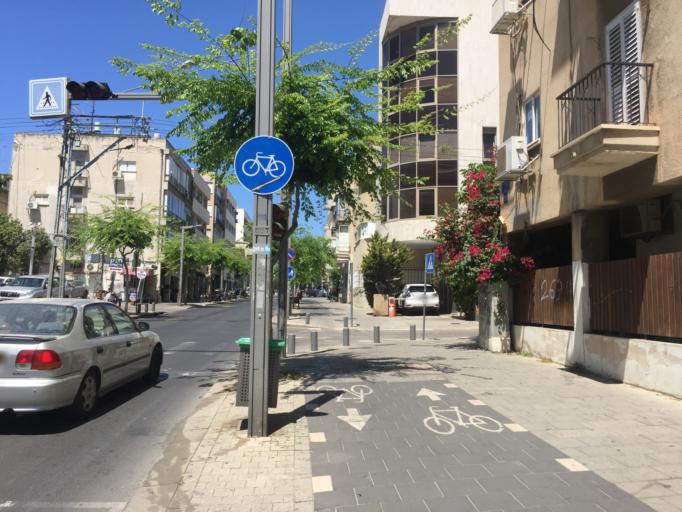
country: IL
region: Tel Aviv
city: Tel Aviv
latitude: 32.0714
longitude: 34.7811
